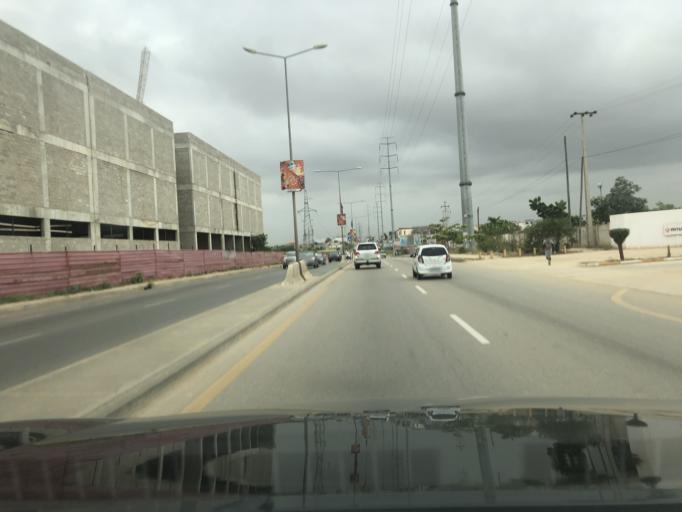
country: AO
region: Luanda
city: Luanda
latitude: -8.9699
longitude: 13.2079
